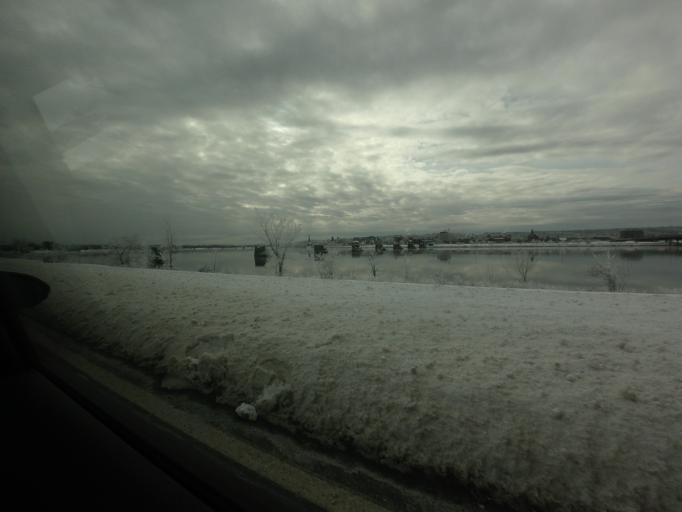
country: CA
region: New Brunswick
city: Fredericton
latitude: 45.9699
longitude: -66.6366
